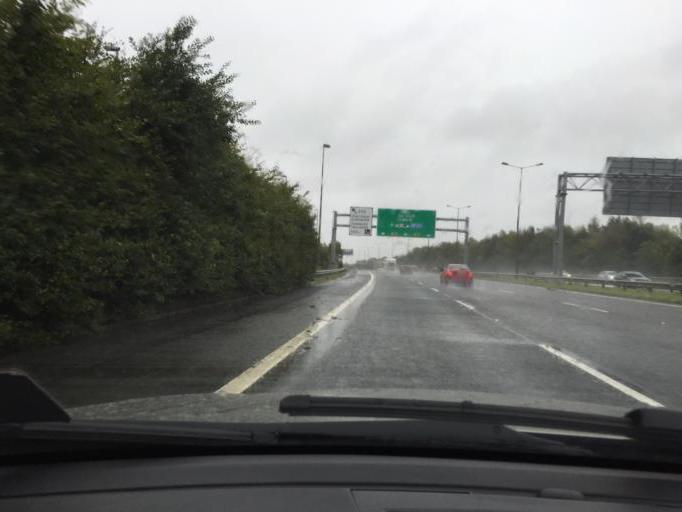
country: IE
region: Leinster
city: Clondalkin
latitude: 53.3064
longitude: -6.4080
